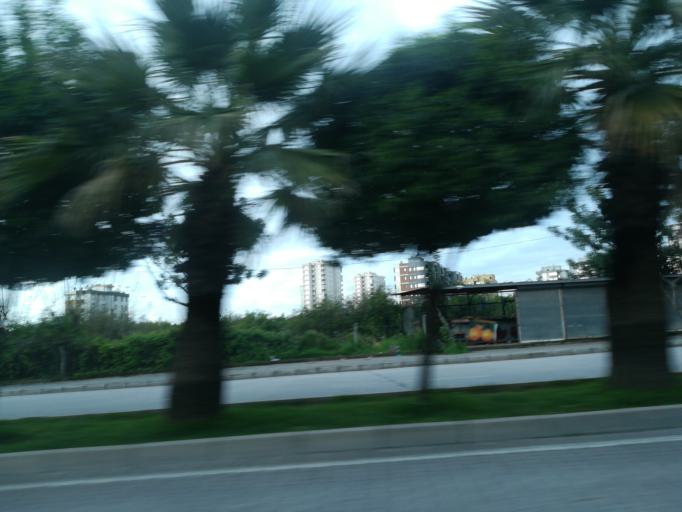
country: TR
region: Adana
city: Seyhan
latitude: 37.0206
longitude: 35.2825
